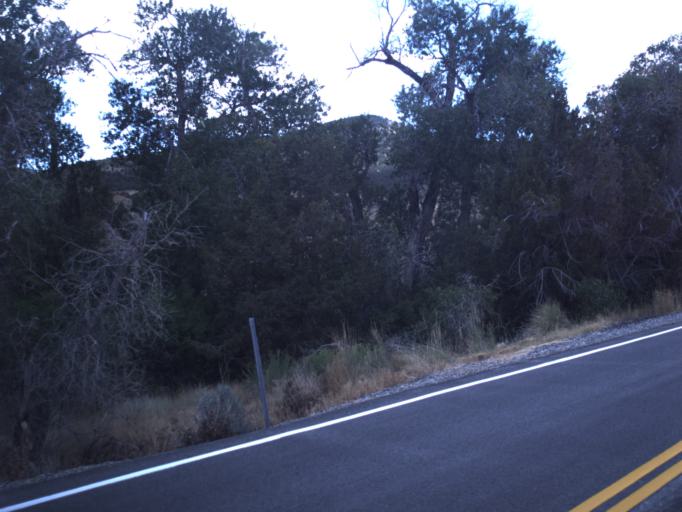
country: US
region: Utah
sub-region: Tooele County
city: Grantsville
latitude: 40.3354
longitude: -112.5281
